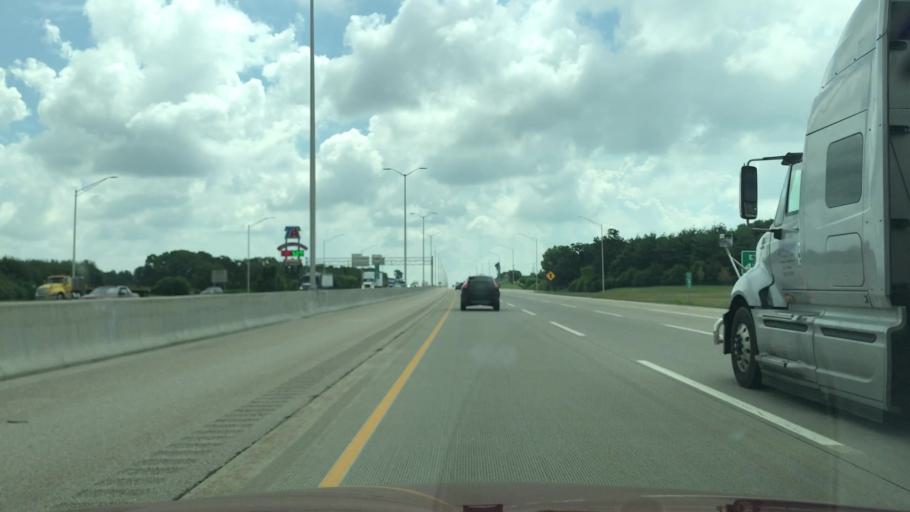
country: US
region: Illinois
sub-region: Kane County
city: Hampshire
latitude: 42.1443
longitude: -88.5139
